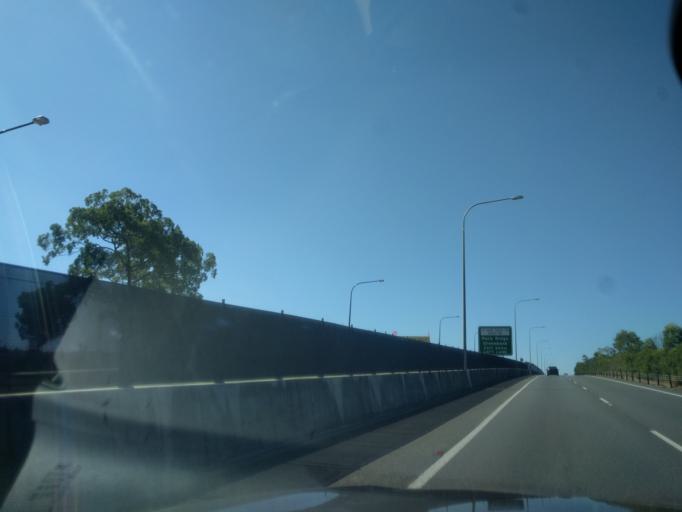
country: AU
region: Queensland
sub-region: Logan
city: Park Ridge South
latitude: -27.7084
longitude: 153.0379
